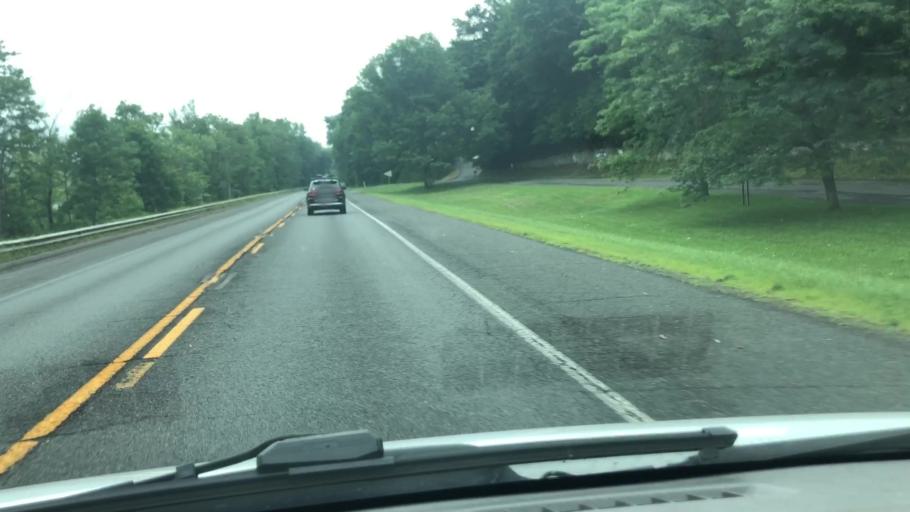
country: US
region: Massachusetts
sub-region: Berkshire County
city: Lanesborough
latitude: 42.5298
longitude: -73.1898
